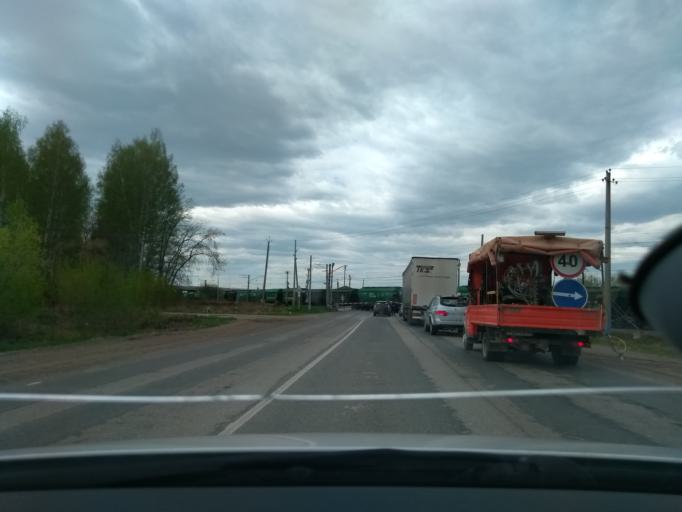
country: RU
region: Perm
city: Lobanovo
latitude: 57.8773
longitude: 56.2725
